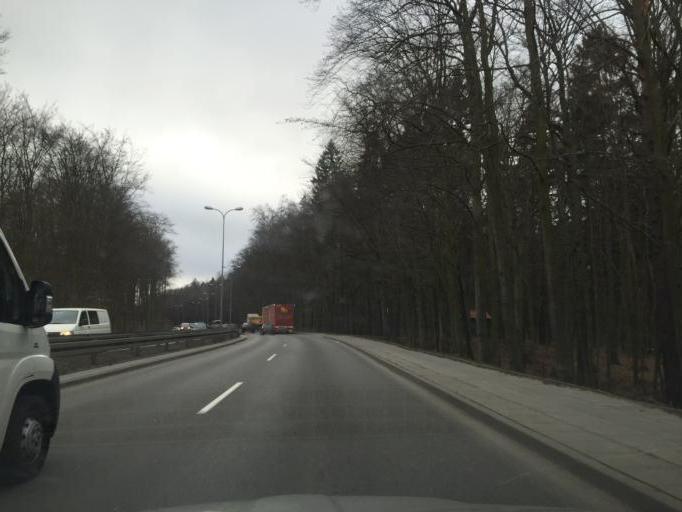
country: PL
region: Pomeranian Voivodeship
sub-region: Sopot
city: Sopot
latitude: 54.3756
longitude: 18.5363
